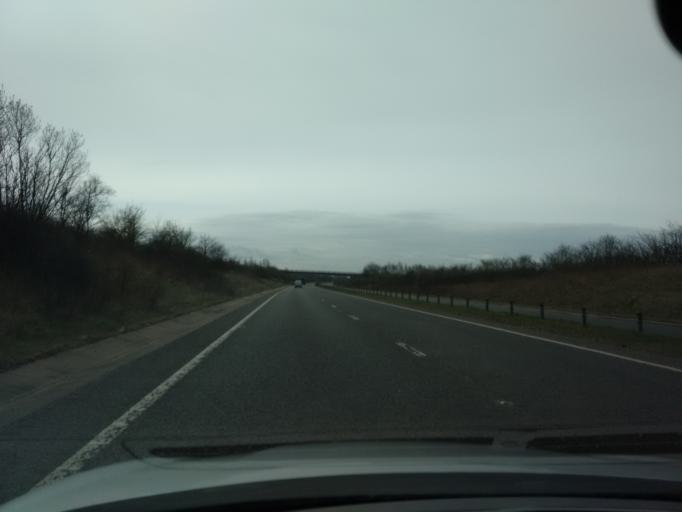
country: GB
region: England
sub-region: Warwickshire
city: Bidford-on-avon
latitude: 52.1808
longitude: -1.8787
